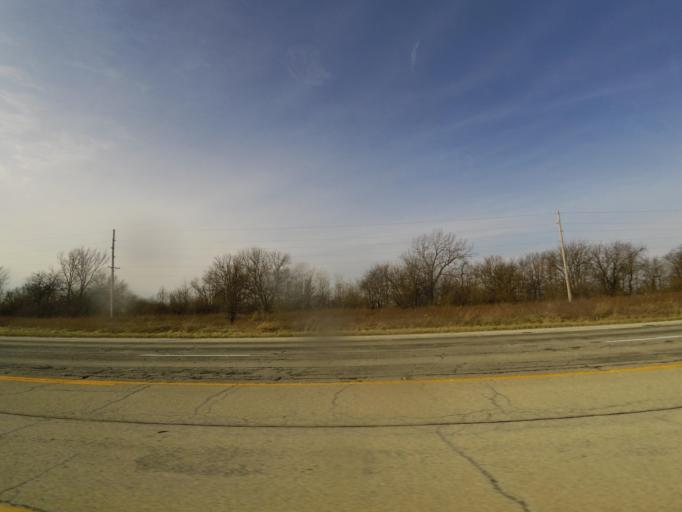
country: US
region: Illinois
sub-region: Macon County
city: Macon
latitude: 39.7722
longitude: -88.9811
